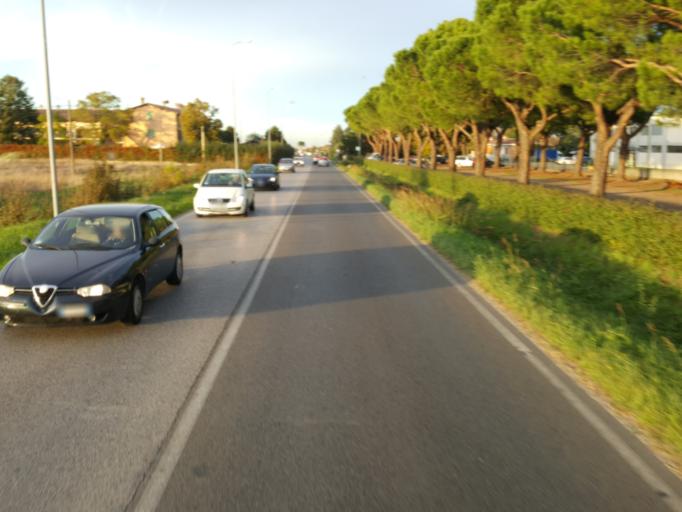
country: IT
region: Emilia-Romagna
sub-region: Provincia di Ravenna
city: Faenza
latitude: 44.2995
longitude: 11.8838
